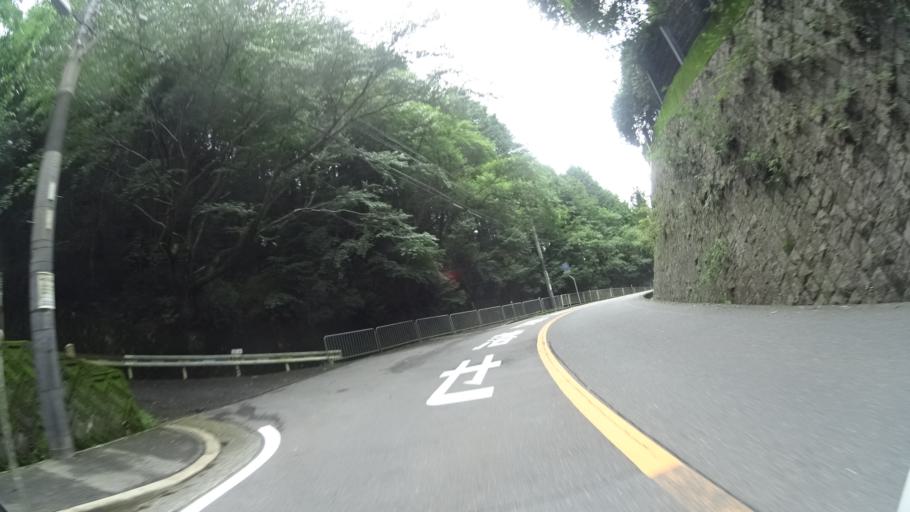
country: JP
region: Kyoto
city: Kameoka
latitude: 34.9678
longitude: 135.4765
